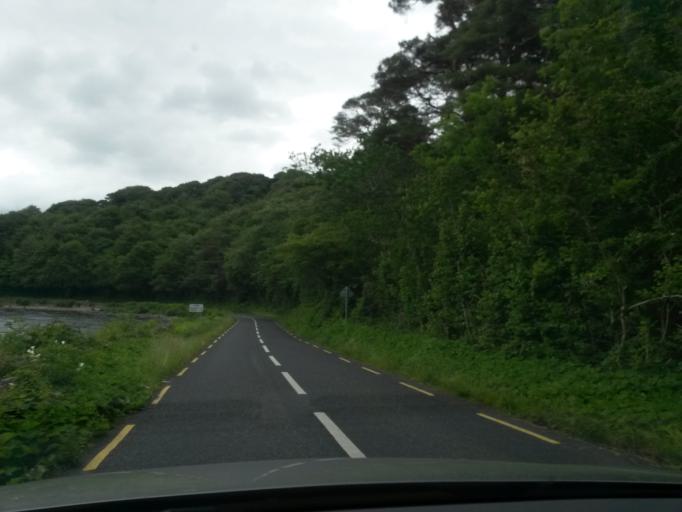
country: IE
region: Connaught
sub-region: County Leitrim
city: Manorhamilton
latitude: 54.2567
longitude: -8.3147
